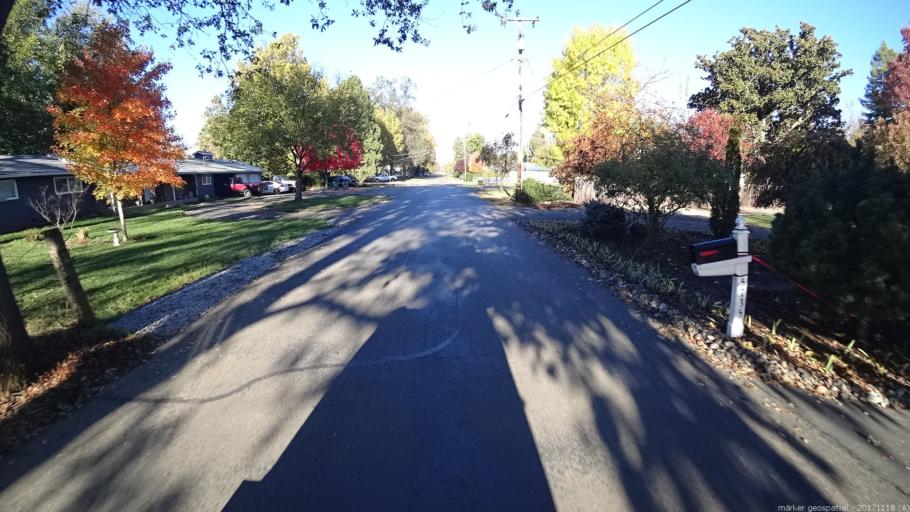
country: US
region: California
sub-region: Shasta County
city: Anderson
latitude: 40.4544
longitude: -122.2397
